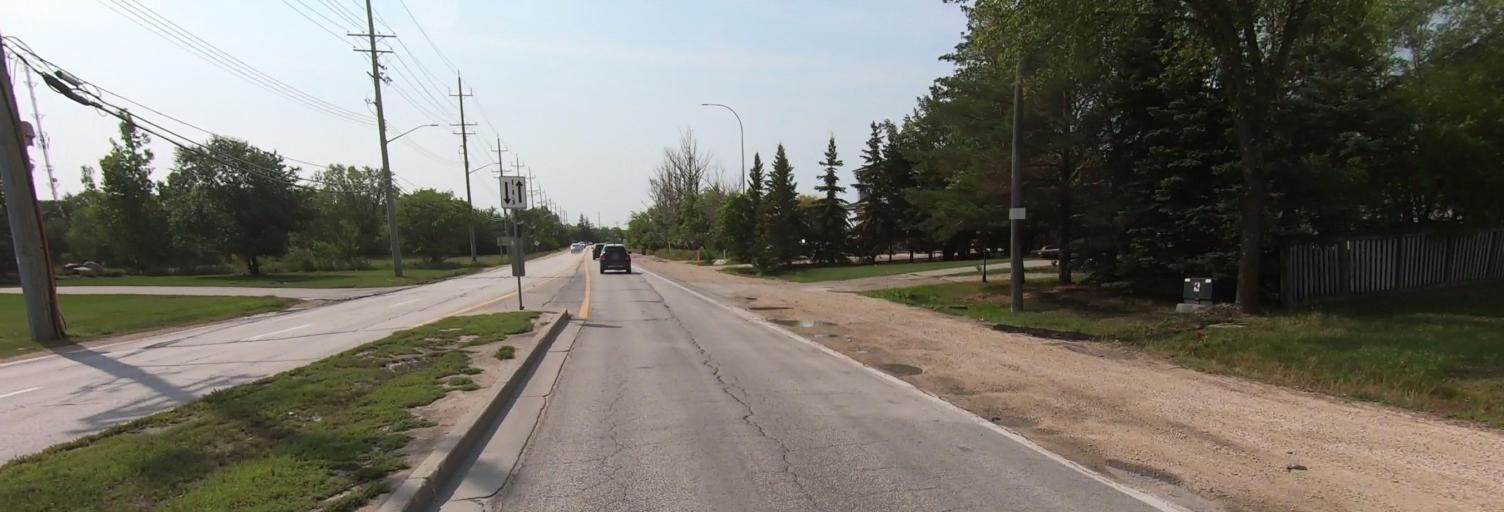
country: CA
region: Manitoba
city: Winnipeg
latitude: 49.8000
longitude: -97.1156
